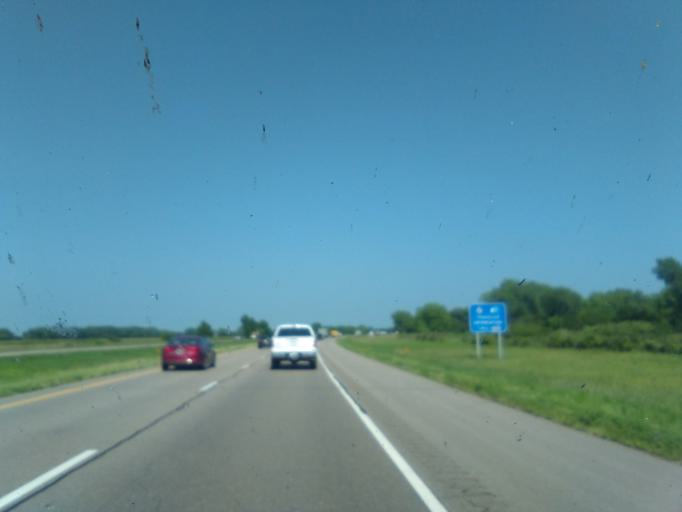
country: US
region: Nebraska
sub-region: Buffalo County
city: Gibbon
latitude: 40.6908
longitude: -98.9345
